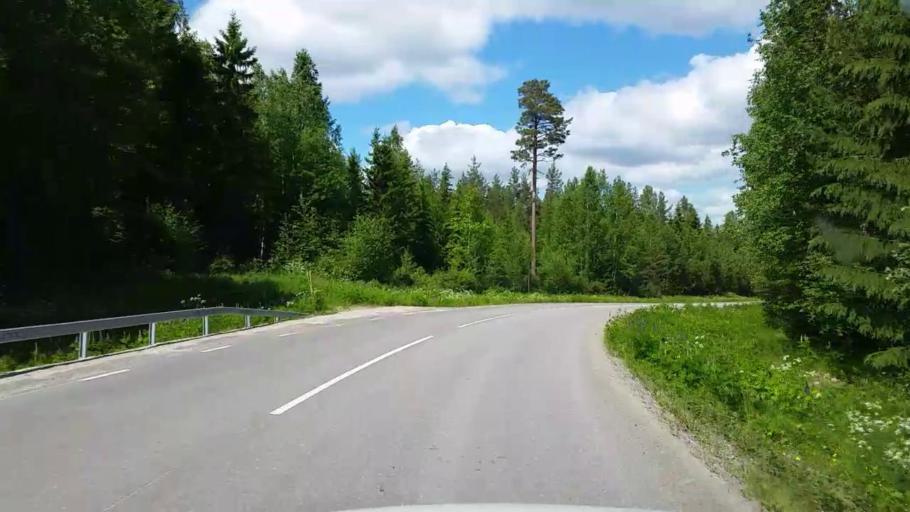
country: SE
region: Gaevleborg
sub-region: Ovanakers Kommun
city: Alfta
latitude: 61.2606
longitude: 16.1219
